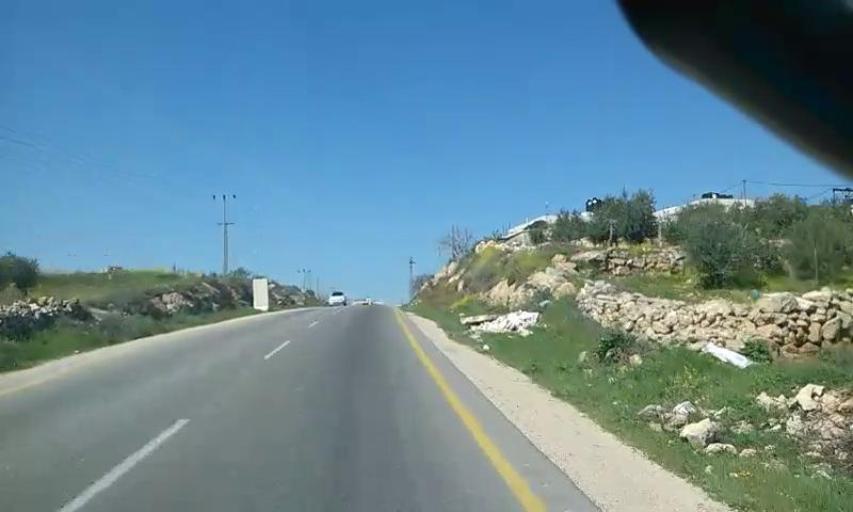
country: PS
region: West Bank
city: Jurat ash Sham`ah
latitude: 31.6489
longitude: 35.1662
